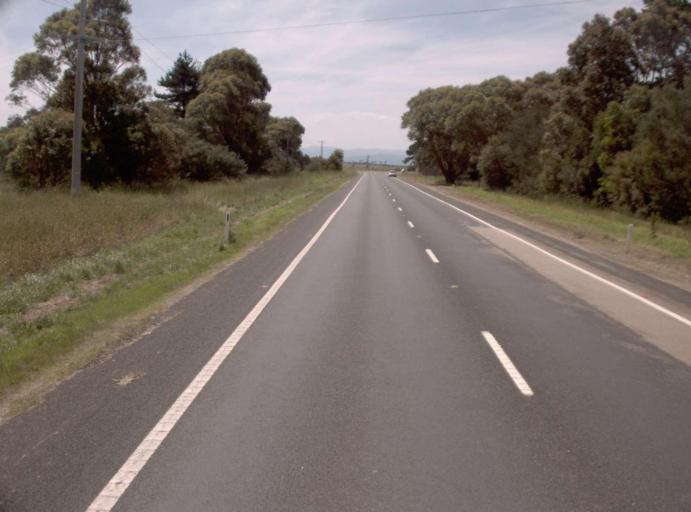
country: AU
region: Victoria
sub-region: Wellington
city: Sale
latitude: -38.0362
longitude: 147.0595
